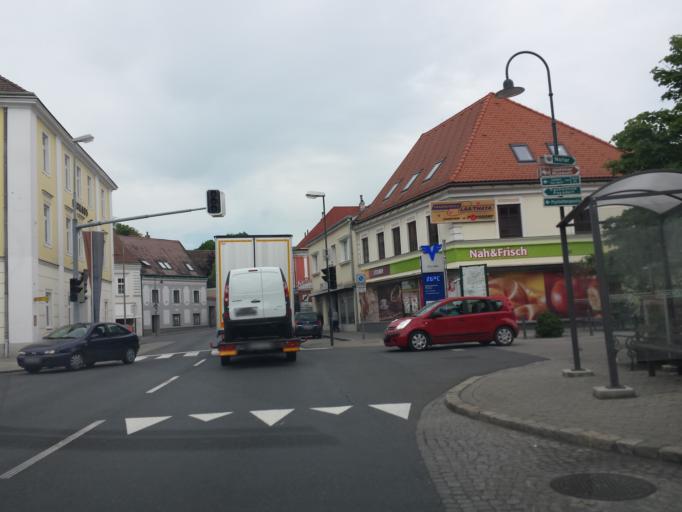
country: AT
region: Lower Austria
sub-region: Politischer Bezirk Mistelbach
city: Poysdorf
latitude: 48.6684
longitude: 16.6295
